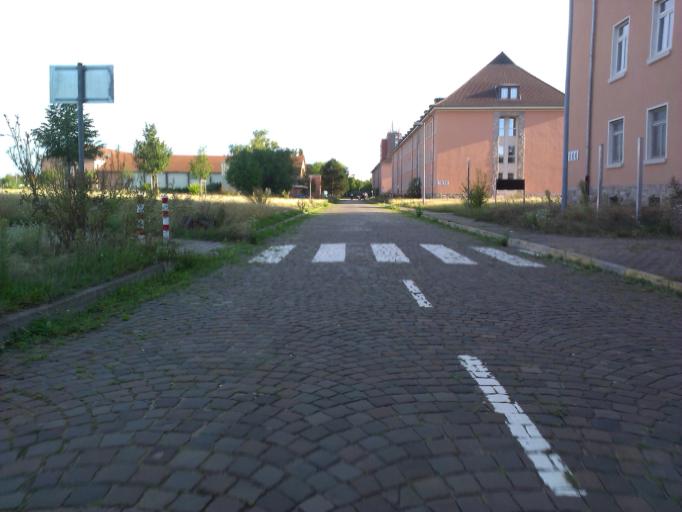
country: DE
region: Baden-Wuerttemberg
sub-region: Karlsruhe Region
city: Mannheim
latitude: 49.4973
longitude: 8.5210
